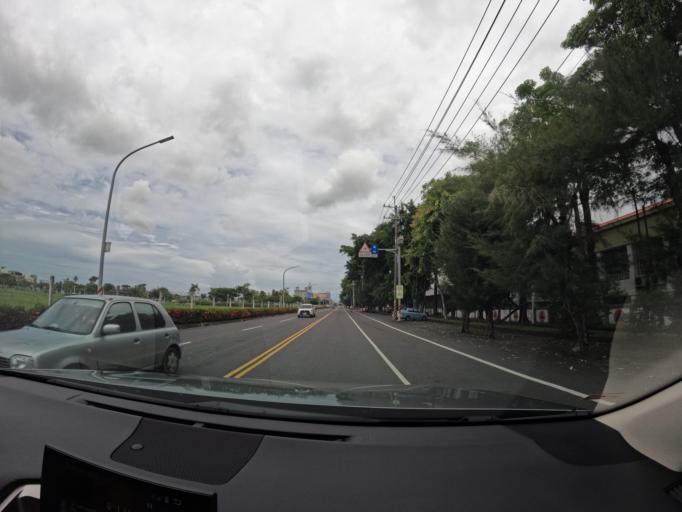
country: TW
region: Kaohsiung
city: Kaohsiung
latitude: 22.7844
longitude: 120.2886
